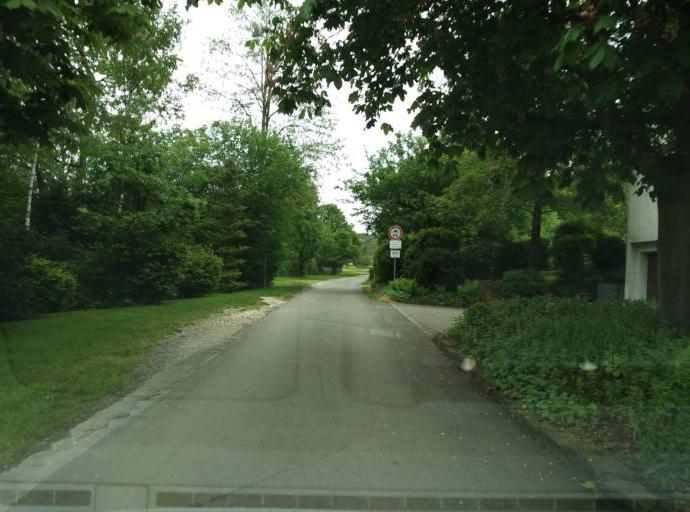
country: DE
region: Baden-Wuerttemberg
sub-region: Regierungsbezirk Stuttgart
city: Frickenhausen
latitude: 48.5877
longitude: 9.3614
